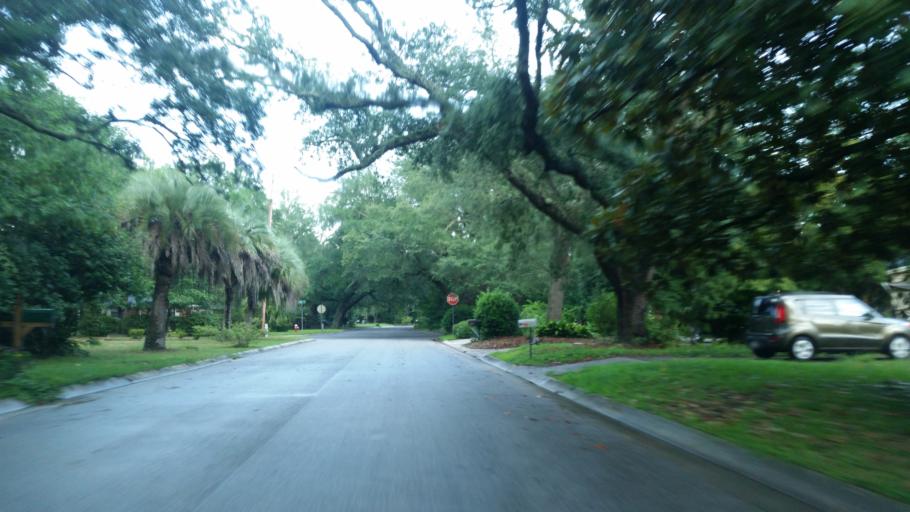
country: US
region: Florida
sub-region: Escambia County
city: Ferry Pass
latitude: 30.4941
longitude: -87.1615
